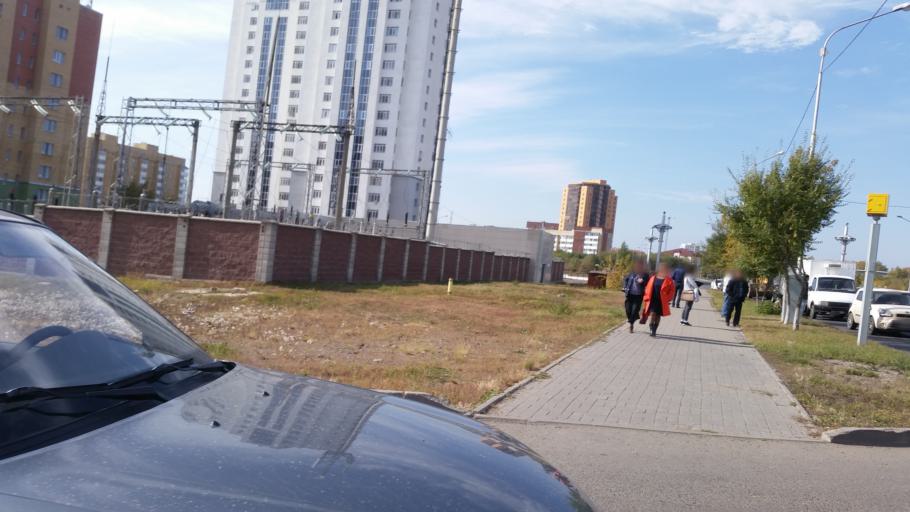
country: KZ
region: Astana Qalasy
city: Astana
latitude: 51.1637
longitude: 71.4799
